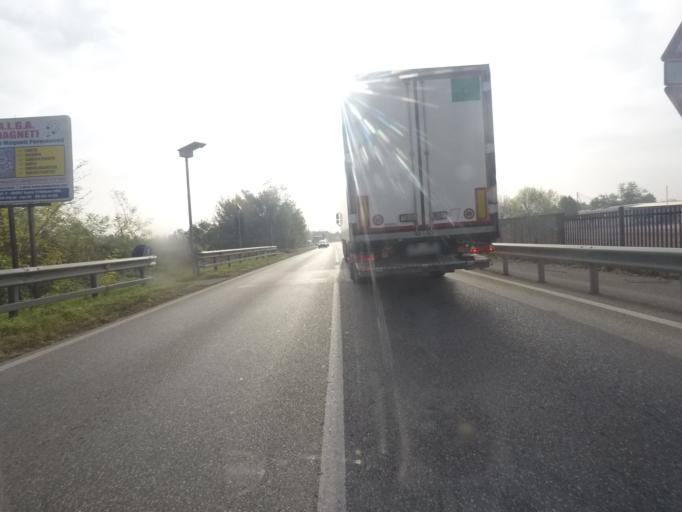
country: IT
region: Lombardy
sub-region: Provincia di Monza e Brianza
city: Vimercate
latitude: 45.6163
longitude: 9.3855
